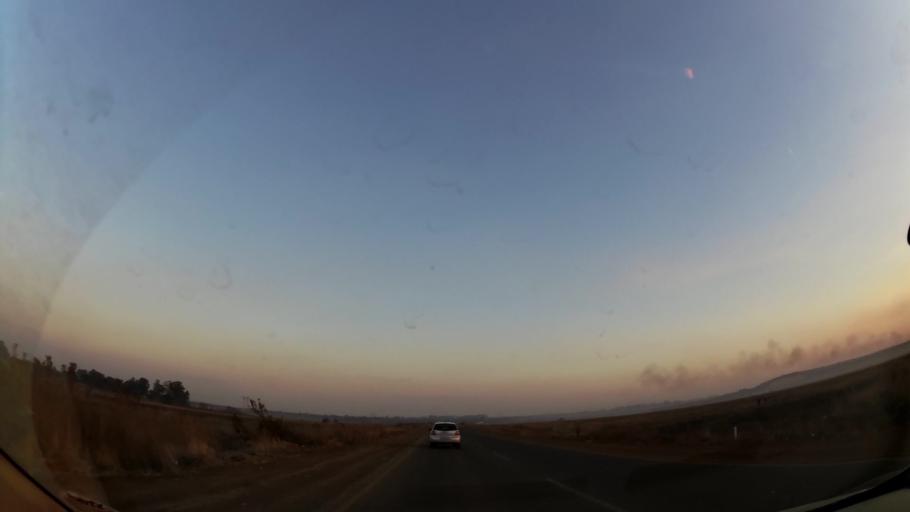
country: ZA
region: Gauteng
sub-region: Ekurhuleni Metropolitan Municipality
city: Springs
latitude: -26.3255
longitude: 28.4241
